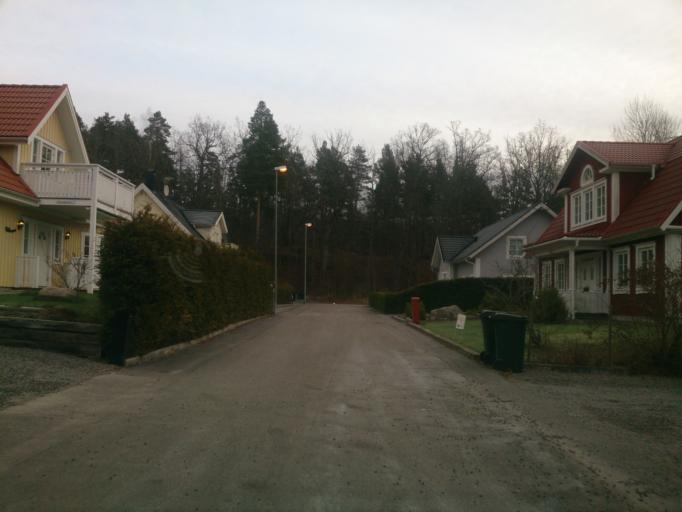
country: SE
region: OEstergoetland
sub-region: Atvidabergs Kommun
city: Atvidaberg
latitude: 58.2038
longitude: 15.9732
